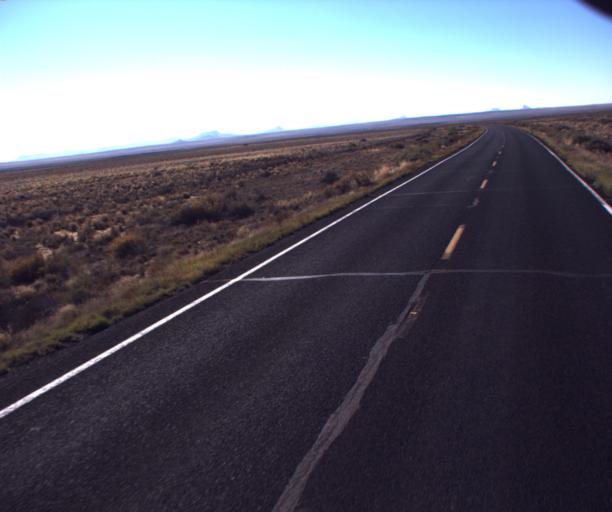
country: US
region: Arizona
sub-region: Navajo County
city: First Mesa
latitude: 35.7355
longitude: -110.5191
